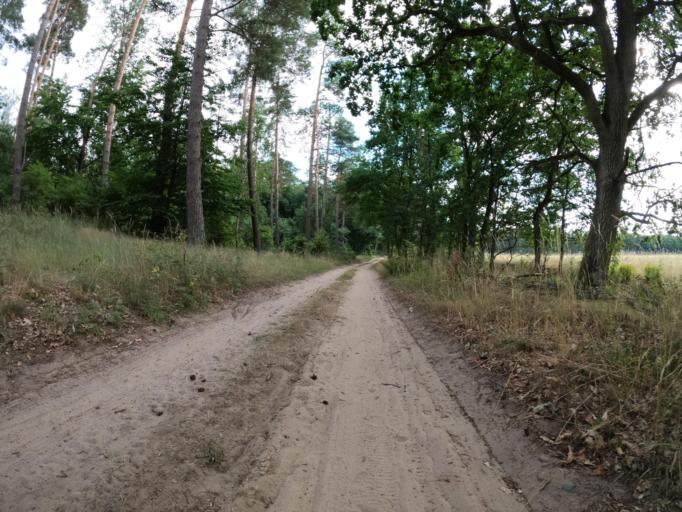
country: DE
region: Brandenburg
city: Lychen
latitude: 53.2655
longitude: 13.4448
